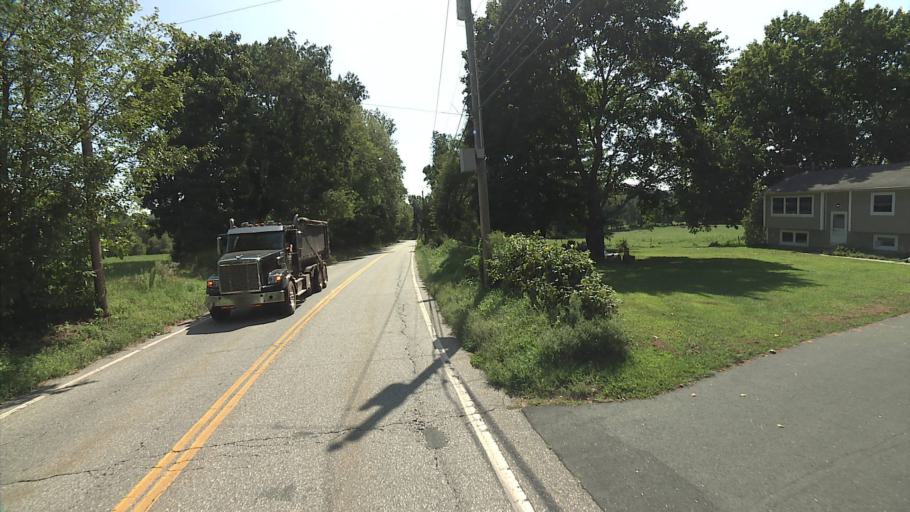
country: US
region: Connecticut
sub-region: Windham County
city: South Windham
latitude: 41.6404
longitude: -72.1815
